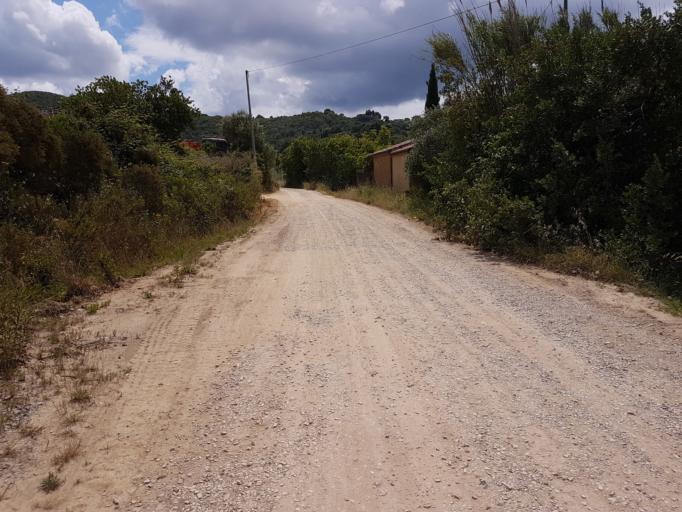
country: IT
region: Tuscany
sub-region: Provincia di Livorno
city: Portoferraio
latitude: 42.7899
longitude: 10.3516
